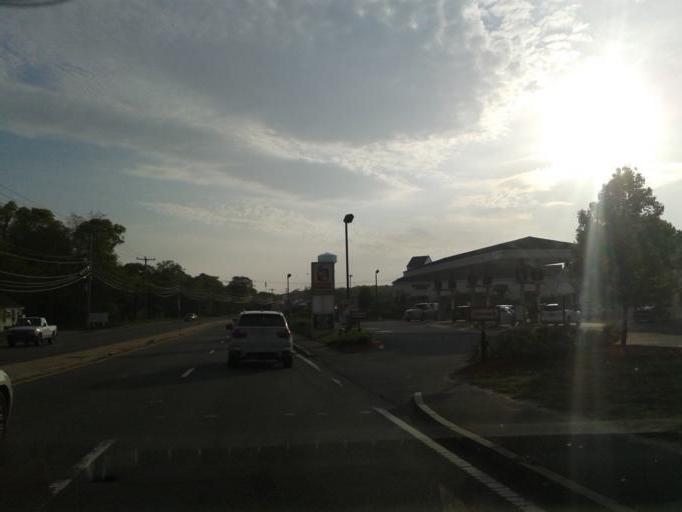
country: US
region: Massachusetts
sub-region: Barnstable County
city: Bourne
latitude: 41.7518
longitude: -70.5926
